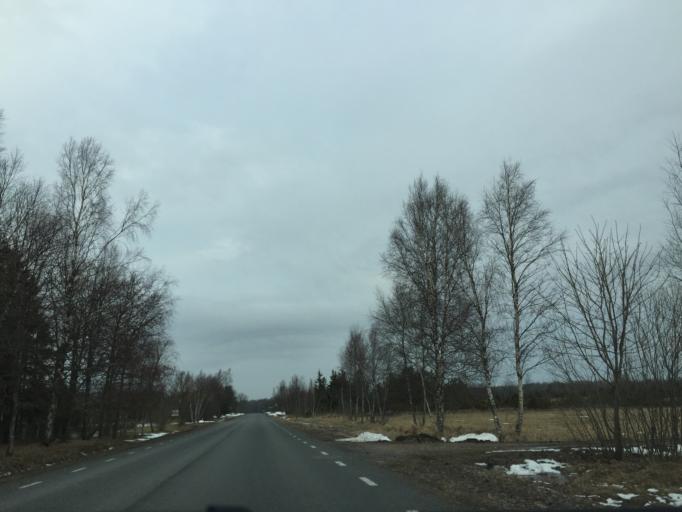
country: EE
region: Saare
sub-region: Kuressaare linn
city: Kuressaare
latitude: 58.4596
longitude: 22.2389
